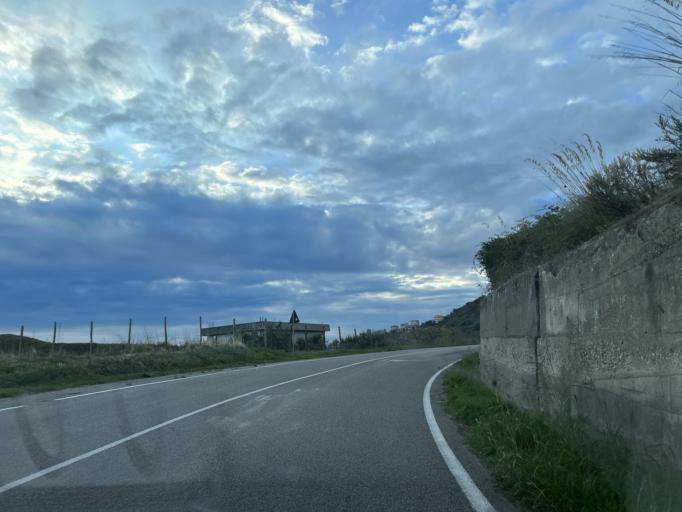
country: IT
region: Calabria
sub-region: Provincia di Catanzaro
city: Montauro
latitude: 38.7563
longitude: 16.5064
